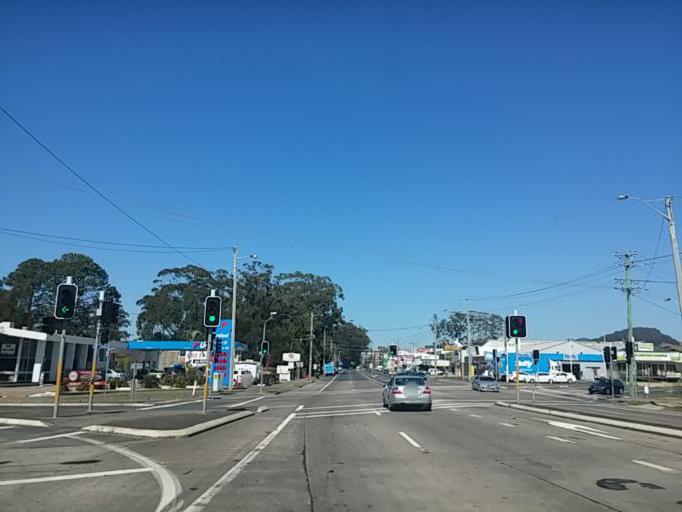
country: AU
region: New South Wales
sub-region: Coffs Harbour
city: Coffs Harbour
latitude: -30.2898
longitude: 153.1216
